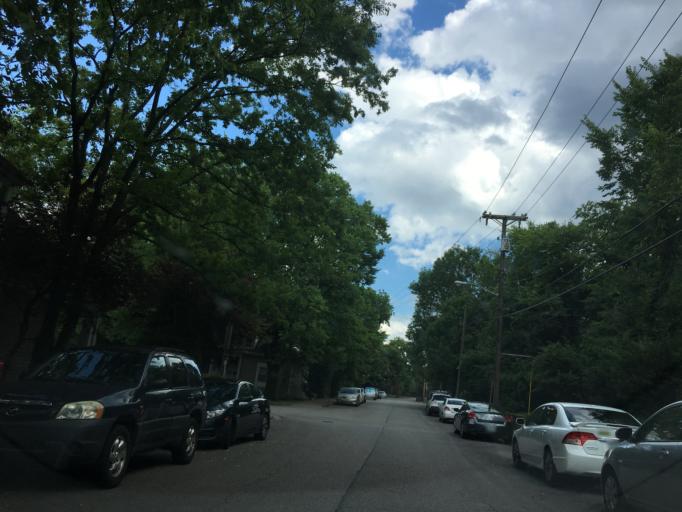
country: US
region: Tennessee
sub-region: Davidson County
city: Nashville
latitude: 36.1396
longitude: -86.8144
